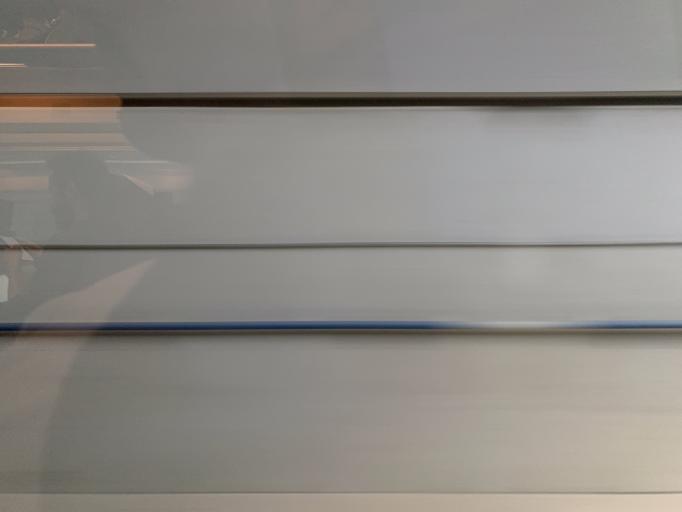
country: ES
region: Catalonia
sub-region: Provincia de Barcelona
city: Sant Sadurni d'Anoia
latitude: 41.4178
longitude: 1.7920
